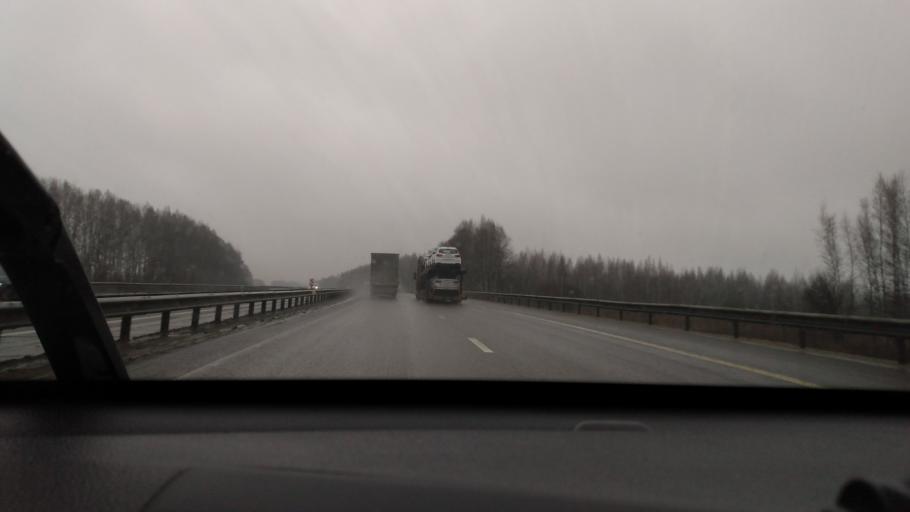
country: RU
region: Tula
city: Shvartsevskiy
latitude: 54.0855
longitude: 38.0419
